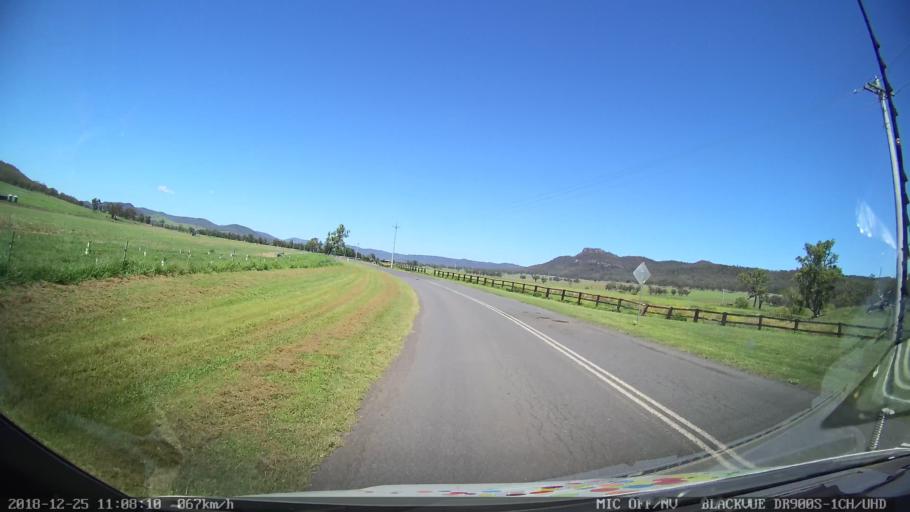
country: AU
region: New South Wales
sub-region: Upper Hunter Shire
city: Merriwa
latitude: -32.4001
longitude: 150.1271
